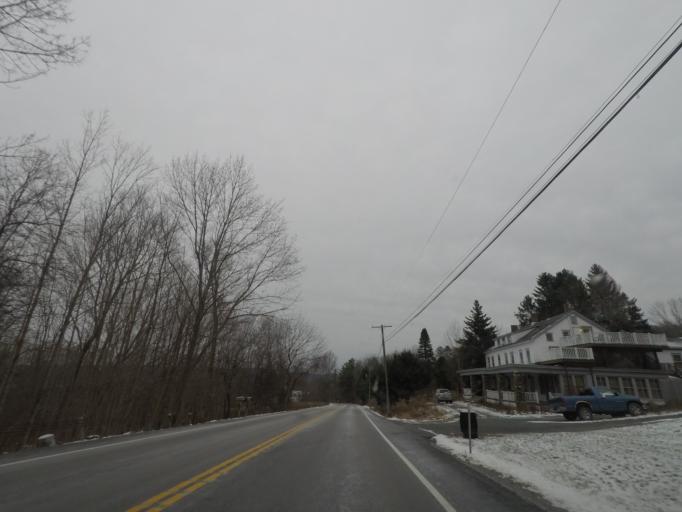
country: US
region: New York
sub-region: Rensselaer County
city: Hoosick Falls
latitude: 42.7680
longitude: -73.4142
